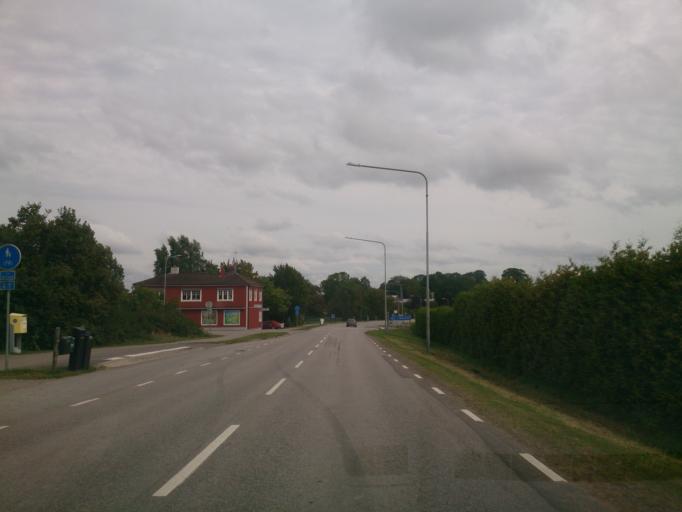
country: SE
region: OEstergoetland
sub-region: Linkopings Kommun
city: Linghem
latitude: 58.4076
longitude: 15.8490
